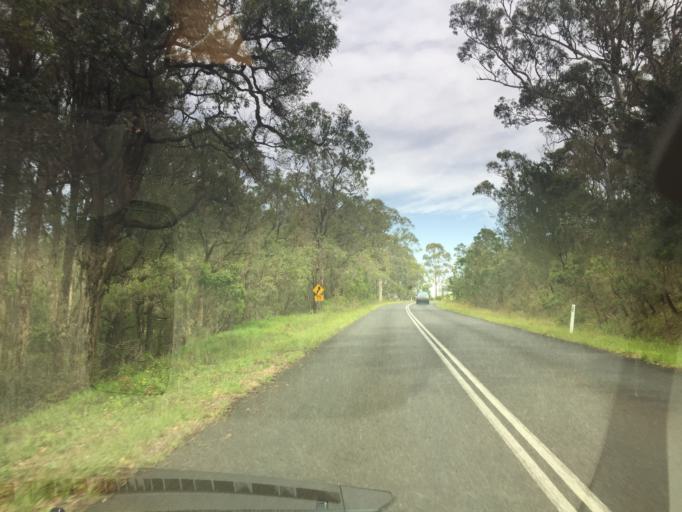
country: AU
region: New South Wales
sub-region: Bega Valley
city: Bega
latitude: -36.7097
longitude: 149.5938
